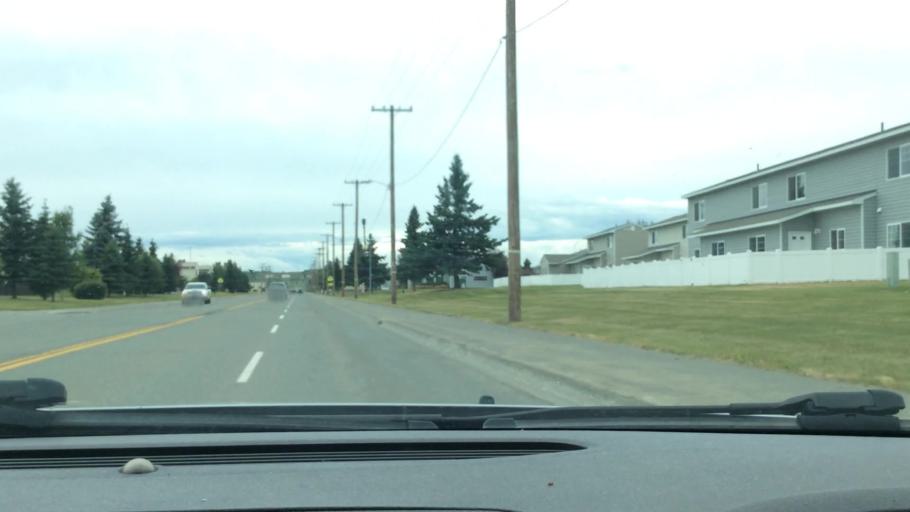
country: US
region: Alaska
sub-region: Anchorage Municipality
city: Anchorage
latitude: 61.2316
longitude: -149.8491
